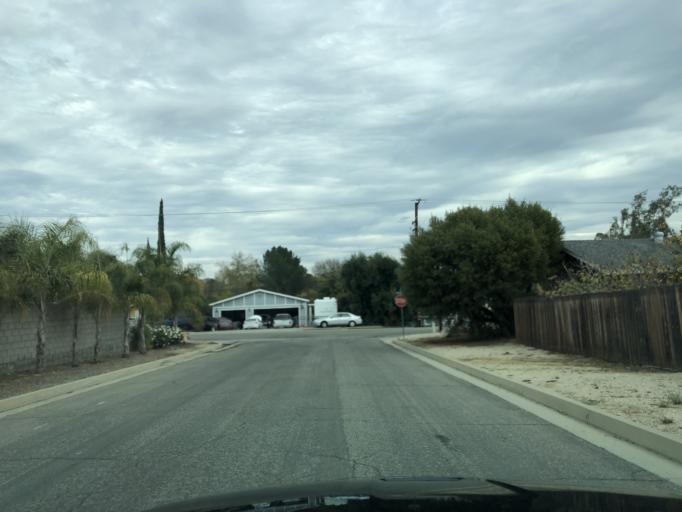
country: US
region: California
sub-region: Riverside County
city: Wildomar
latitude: 33.6063
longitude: -117.2853
